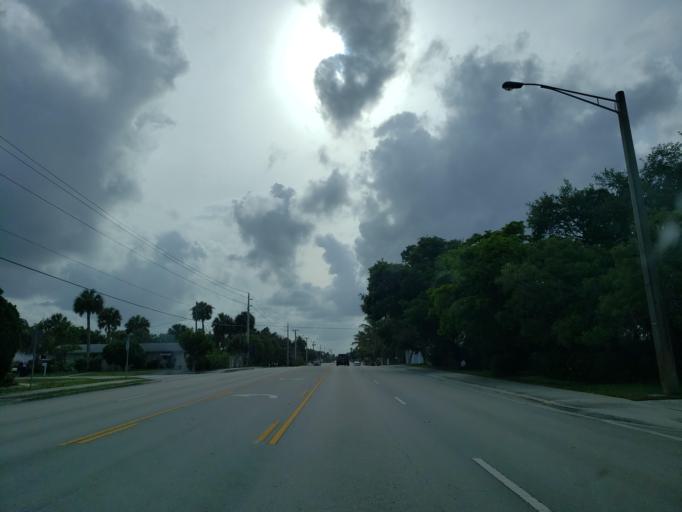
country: US
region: Florida
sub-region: Martin County
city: Stuart
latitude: 27.1975
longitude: -80.2298
